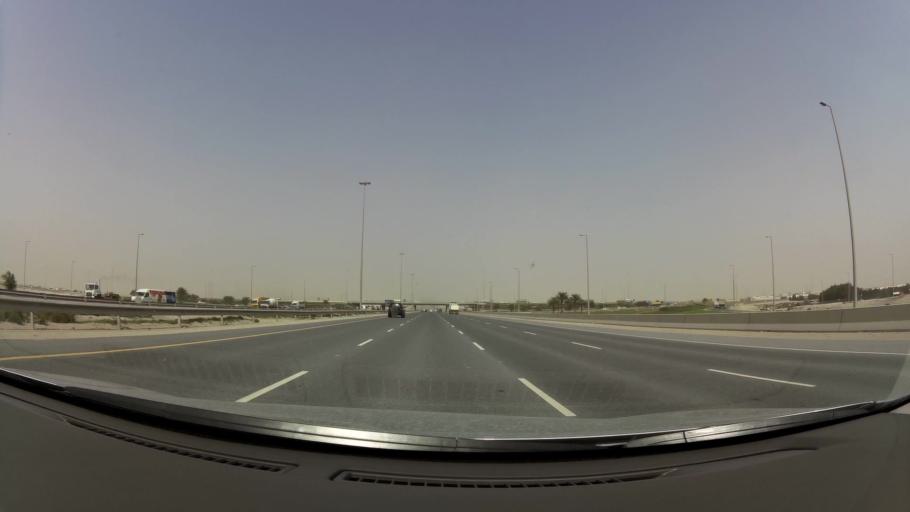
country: QA
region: Baladiyat ar Rayyan
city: Ar Rayyan
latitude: 25.1967
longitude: 51.3823
